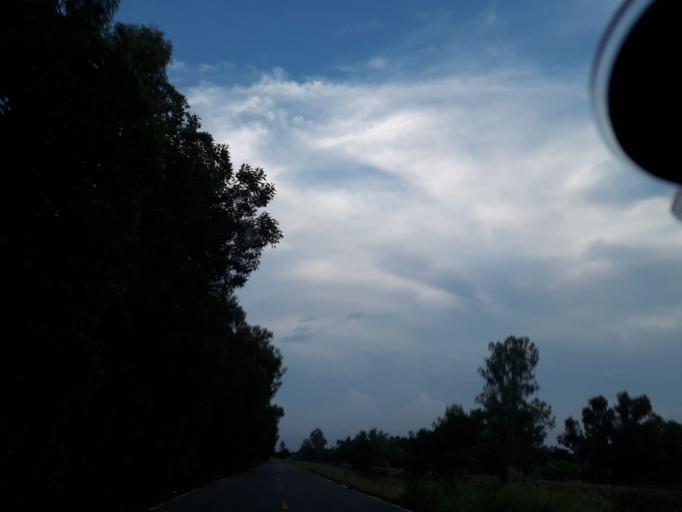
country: TH
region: Pathum Thani
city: Nong Suea
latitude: 14.2156
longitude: 100.8689
